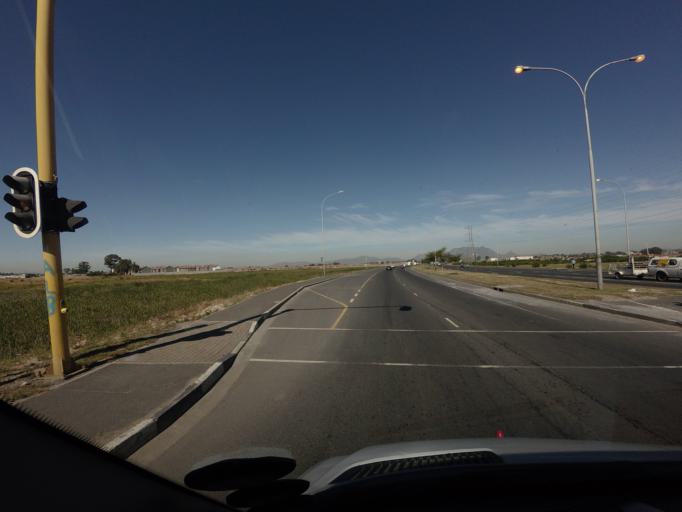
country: ZA
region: Western Cape
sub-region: City of Cape Town
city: Kraaifontein
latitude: -33.9560
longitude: 18.6872
